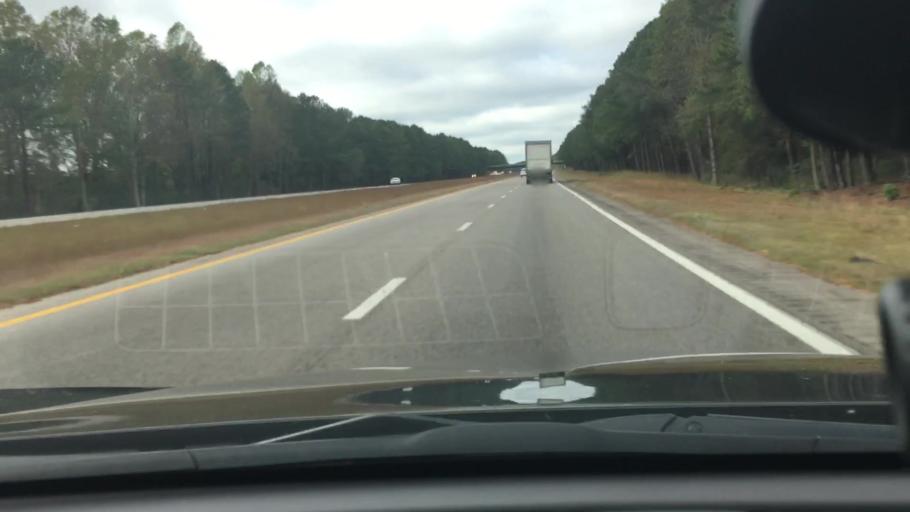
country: US
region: North Carolina
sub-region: Wilson County
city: Lucama
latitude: 35.7798
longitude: -78.0796
